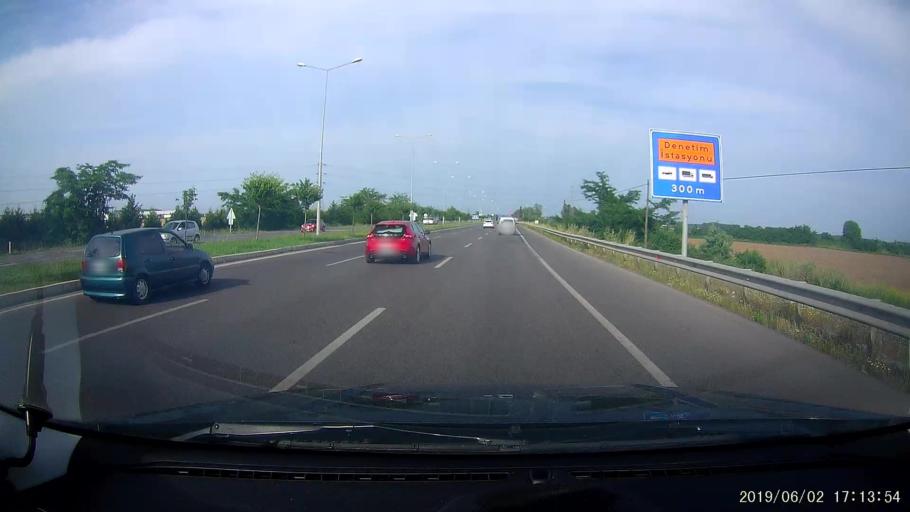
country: TR
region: Samsun
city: Tekkekoy
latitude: 41.2329
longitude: 36.5185
